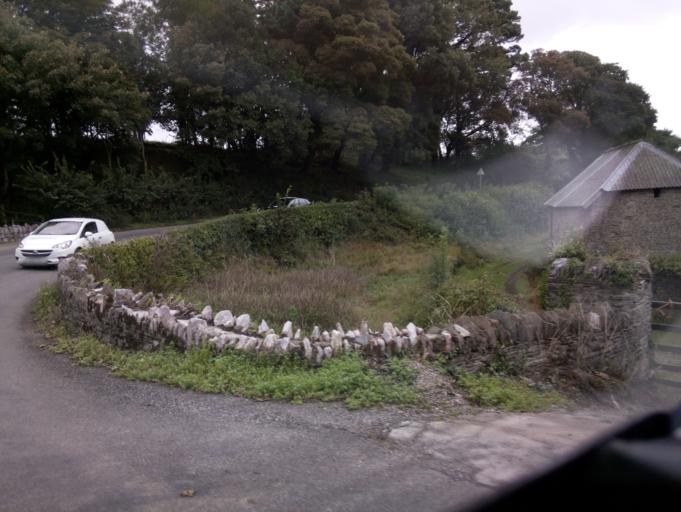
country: GB
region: England
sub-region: Devon
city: Dartmouth
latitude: 50.3150
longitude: -3.6258
